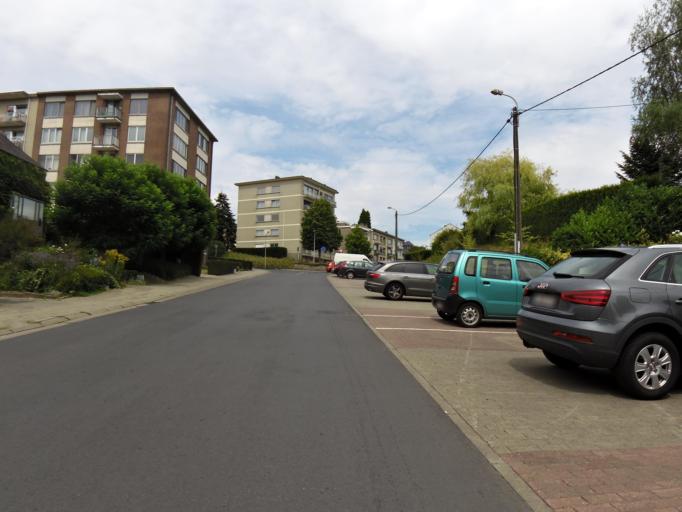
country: BE
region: Flanders
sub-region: Provincie Vlaams-Brabant
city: Dilbeek
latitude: 50.8410
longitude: 4.2583
